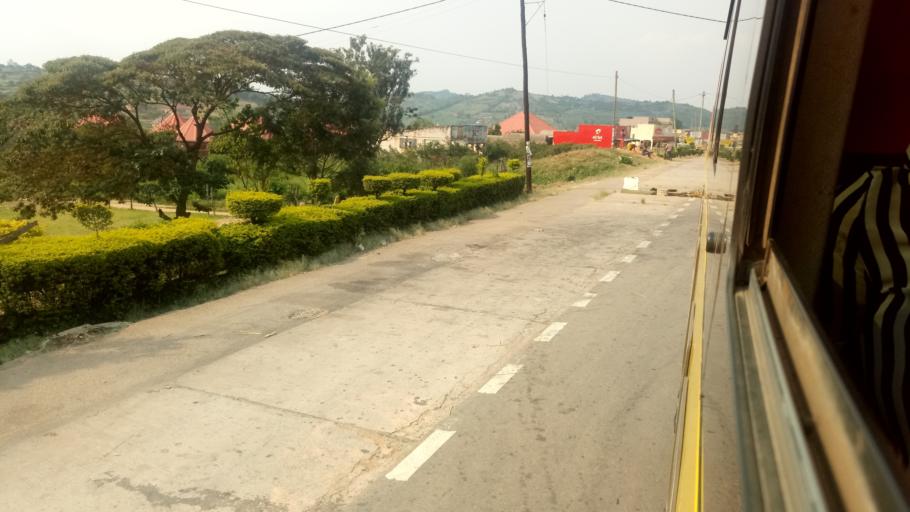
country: UG
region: Western Region
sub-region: Mbarara District
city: Mbarara
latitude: -0.5255
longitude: 30.7295
